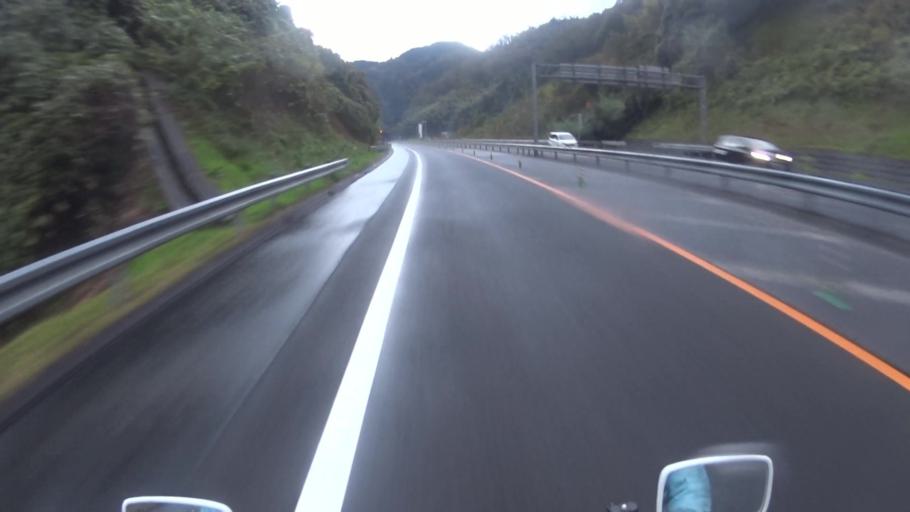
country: JP
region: Kyoto
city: Miyazu
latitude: 35.4188
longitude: 135.2145
